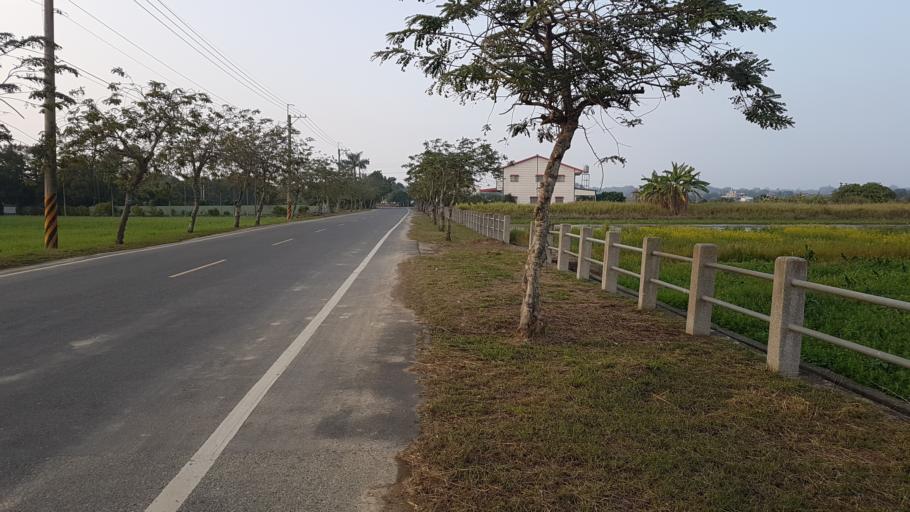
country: TW
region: Taiwan
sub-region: Chiayi
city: Jiayi Shi
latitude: 23.3712
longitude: 120.4501
